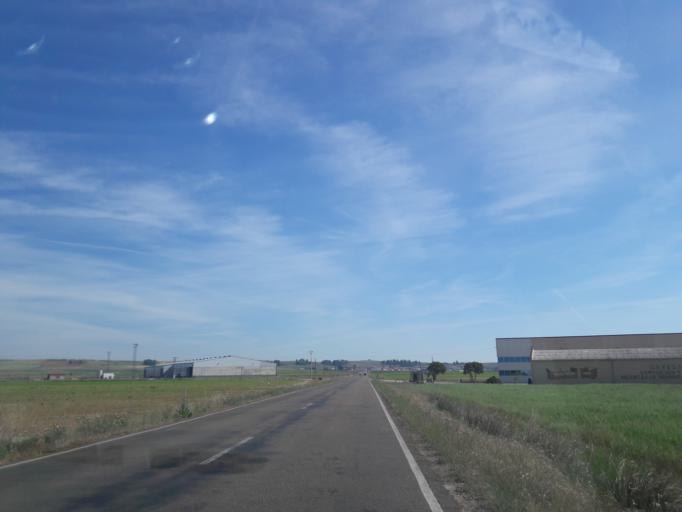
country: ES
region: Castille and Leon
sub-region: Provincia de Salamanca
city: Babilafuente
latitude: 40.9863
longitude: -5.4070
